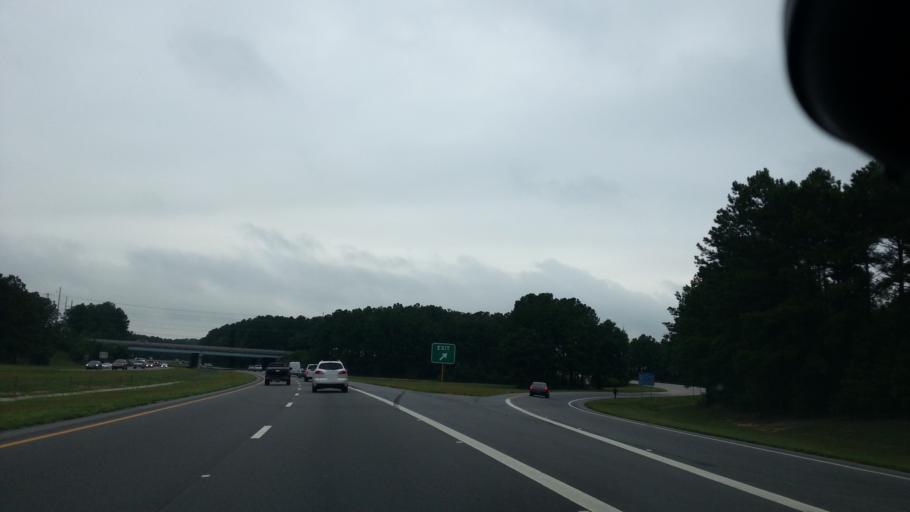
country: US
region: North Carolina
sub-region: Cumberland County
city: Fort Bragg
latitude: 35.0747
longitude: -78.9577
